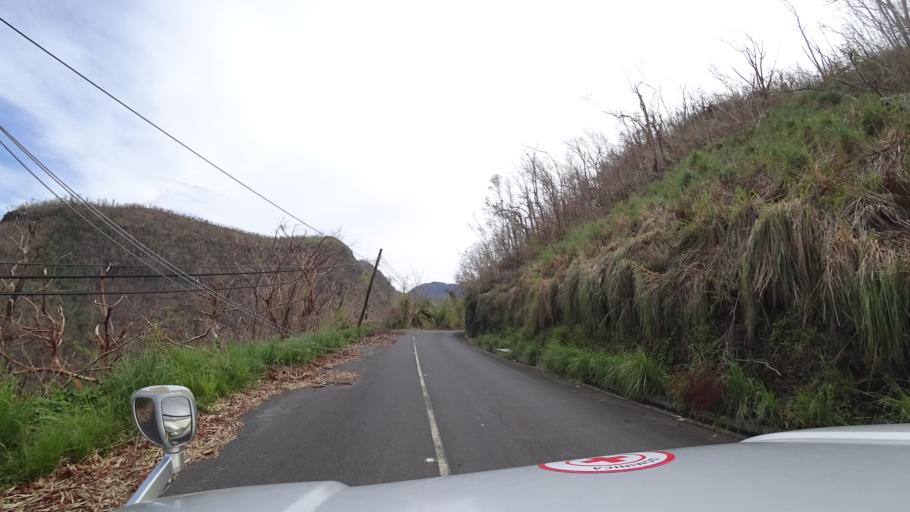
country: DM
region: Saint Paul
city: Mahaut
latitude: 15.3405
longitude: -61.3820
